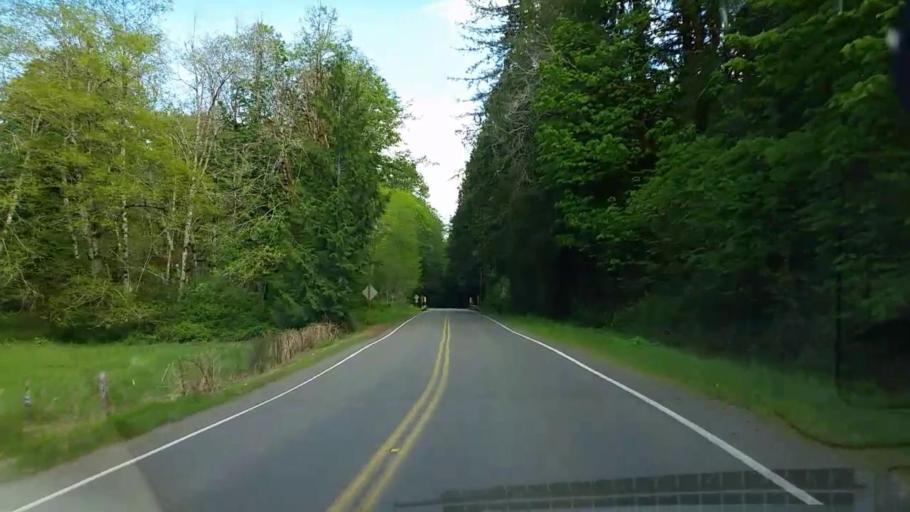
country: US
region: Washington
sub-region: Mason County
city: Shelton
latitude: 47.3160
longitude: -123.2568
